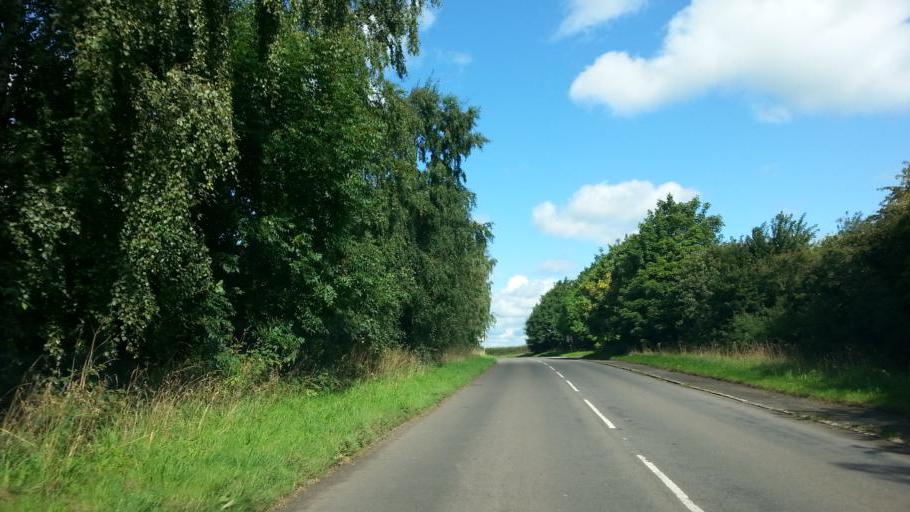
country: GB
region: England
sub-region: Staffordshire
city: Rugeley
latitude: 52.8234
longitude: -1.8932
